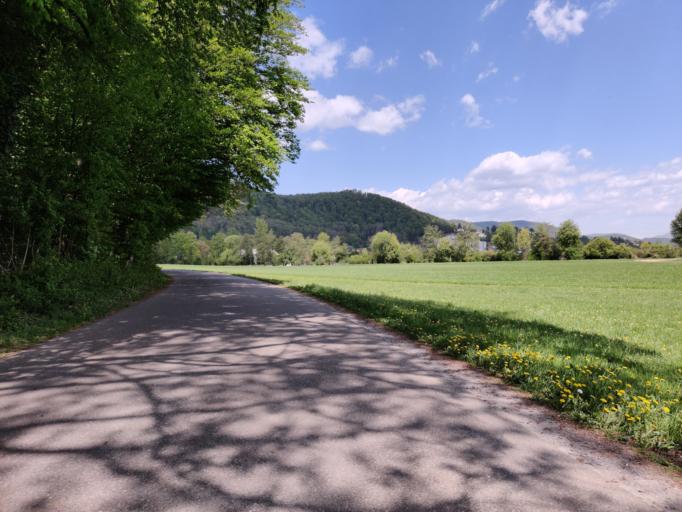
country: AT
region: Styria
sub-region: Graz Stadt
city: Wetzelsdorf
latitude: 47.0384
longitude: 15.3893
